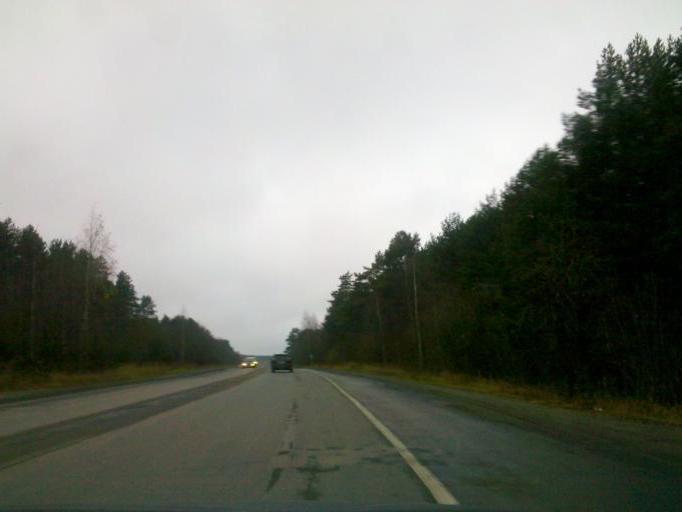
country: RU
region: Republic of Karelia
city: Shuya
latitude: 61.8576
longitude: 34.1749
